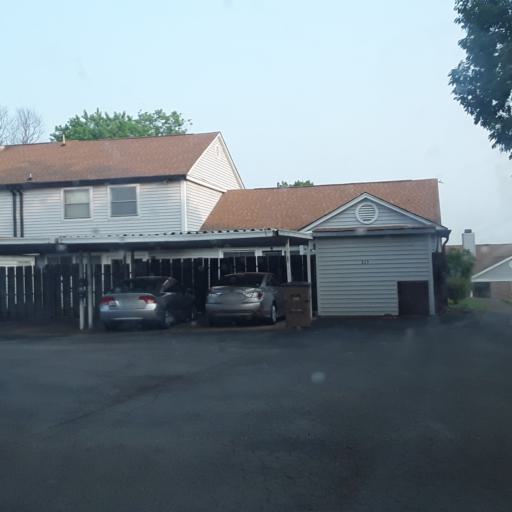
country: US
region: Tennessee
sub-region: Williamson County
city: Brentwood Estates
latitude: 36.0502
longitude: -86.7273
